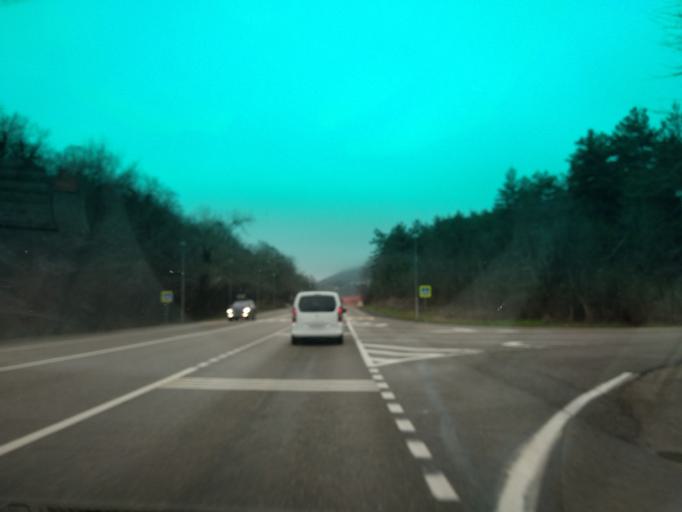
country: RU
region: Krasnodarskiy
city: Ol'ginka
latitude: 44.1883
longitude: 38.8913
